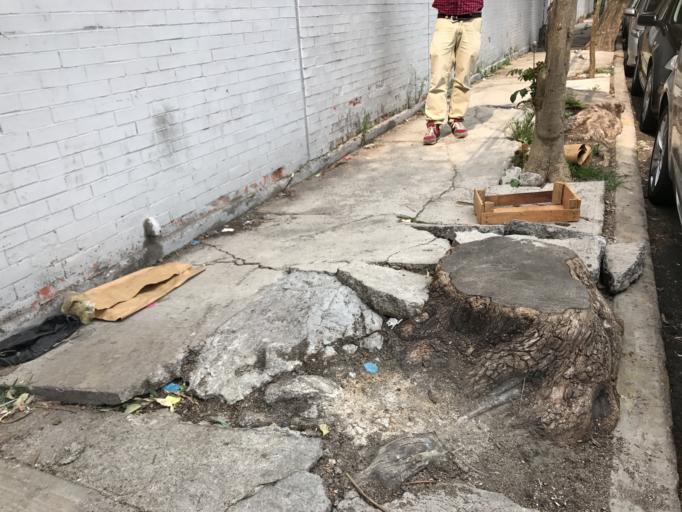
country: MX
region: Mexico City
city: Tlalpan
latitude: 19.2900
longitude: -99.1389
